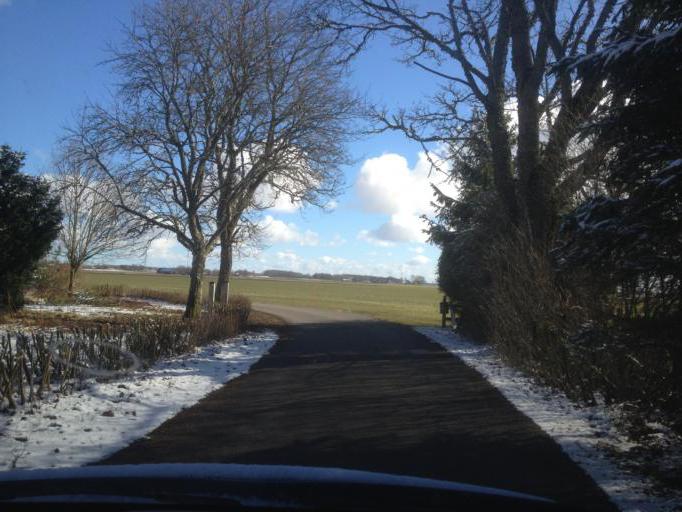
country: SE
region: OEstergoetland
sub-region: Mjolby Kommun
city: Mantorp
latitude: 58.4470
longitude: 15.3326
